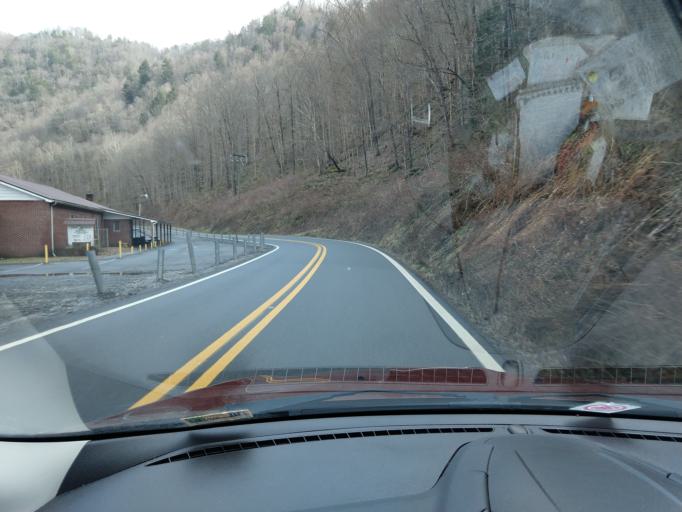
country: US
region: West Virginia
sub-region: McDowell County
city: Welch
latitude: 37.3397
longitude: -81.7454
